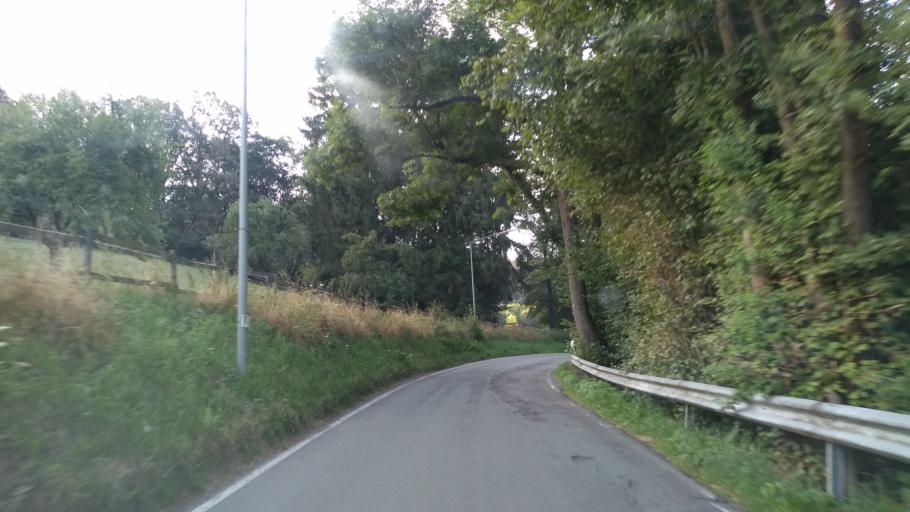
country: DE
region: North Rhine-Westphalia
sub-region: Regierungsbezirk Koln
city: Gummersbach
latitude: 51.0338
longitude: 7.5316
